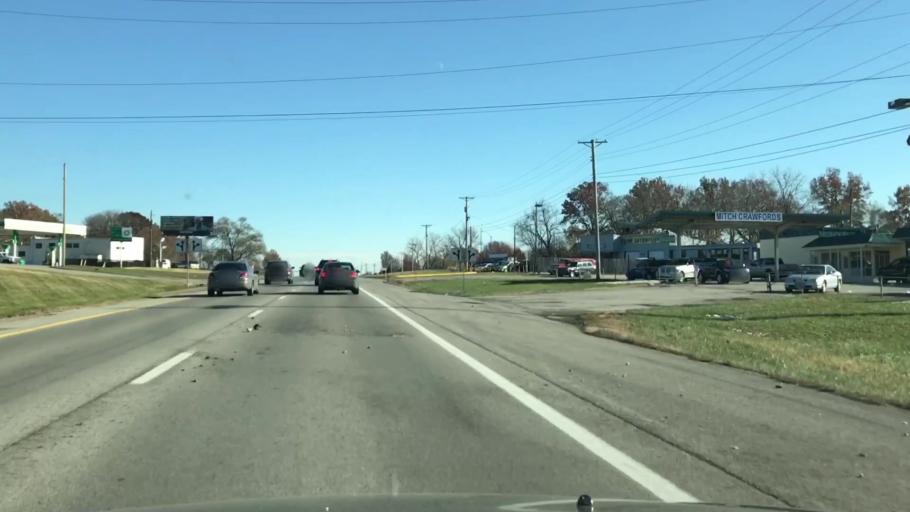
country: US
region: Missouri
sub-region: Jackson County
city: Raytown
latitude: 38.9803
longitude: -94.4555
